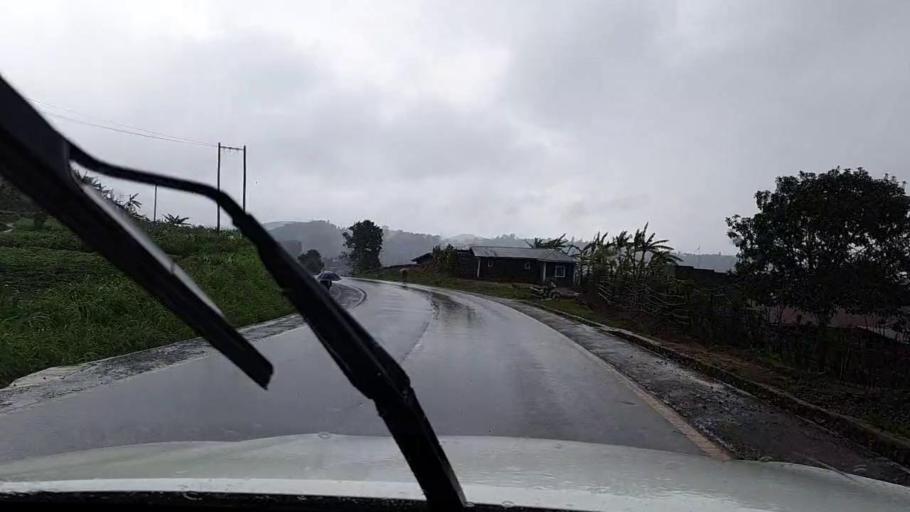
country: RW
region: Western Province
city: Cyangugu
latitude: -2.4623
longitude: 28.9876
